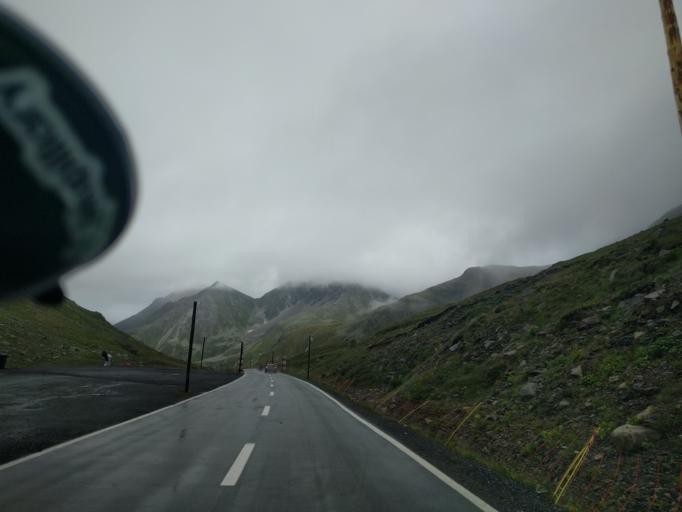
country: CH
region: Grisons
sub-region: Praettigau/Davos District
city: Davos
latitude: 46.7454
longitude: 9.9573
